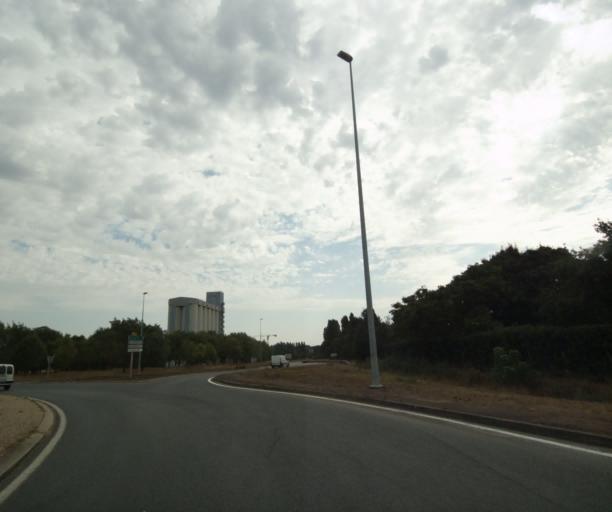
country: FR
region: Poitou-Charentes
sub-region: Departement de la Charente-Maritime
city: Tonnay-Charente
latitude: 45.9530
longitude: -0.8783
